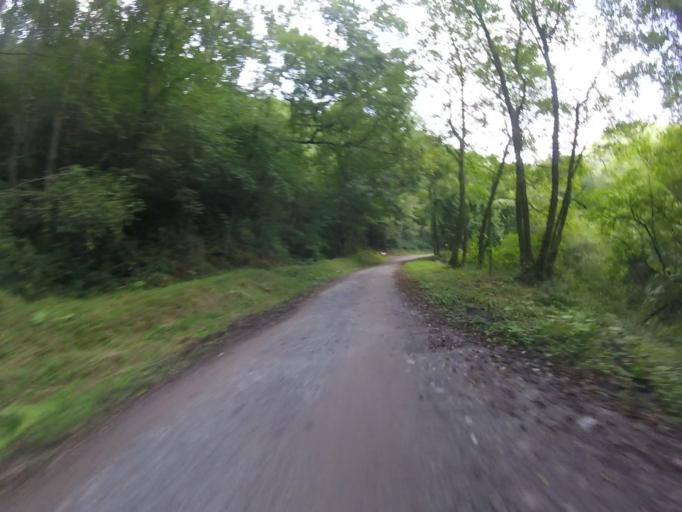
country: ES
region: Basque Country
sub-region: Provincia de Guipuzcoa
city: Andoain
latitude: 43.1862
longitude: -1.9952
